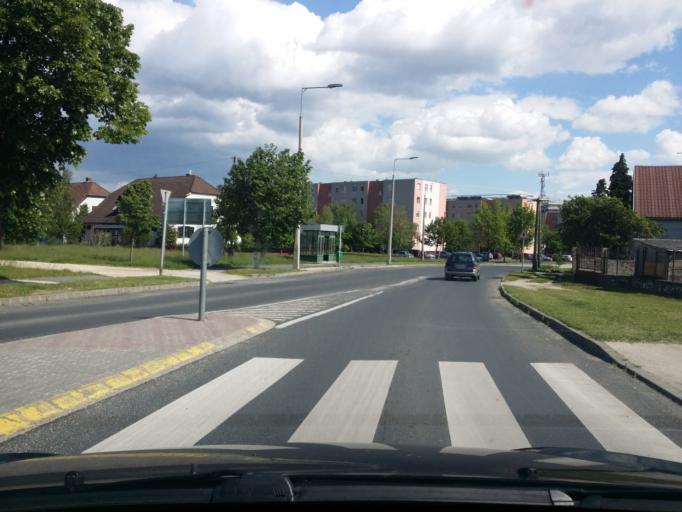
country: HU
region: Veszprem
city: Tapolca
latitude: 46.8887
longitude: 17.4466
